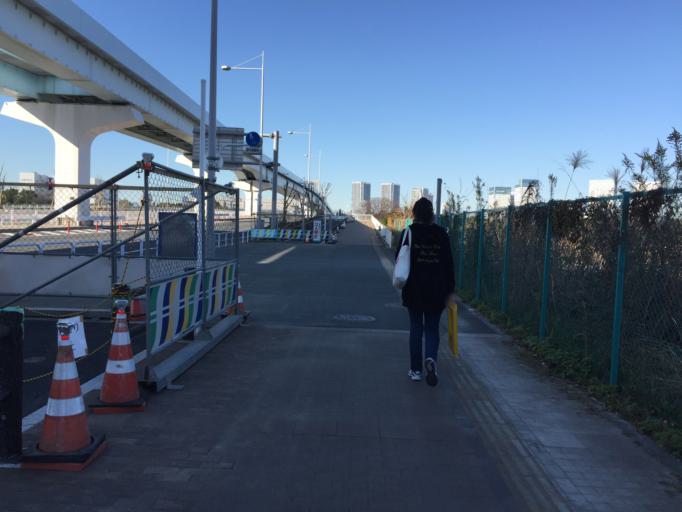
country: JP
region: Tokyo
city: Urayasu
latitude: 35.6403
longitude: 139.7889
